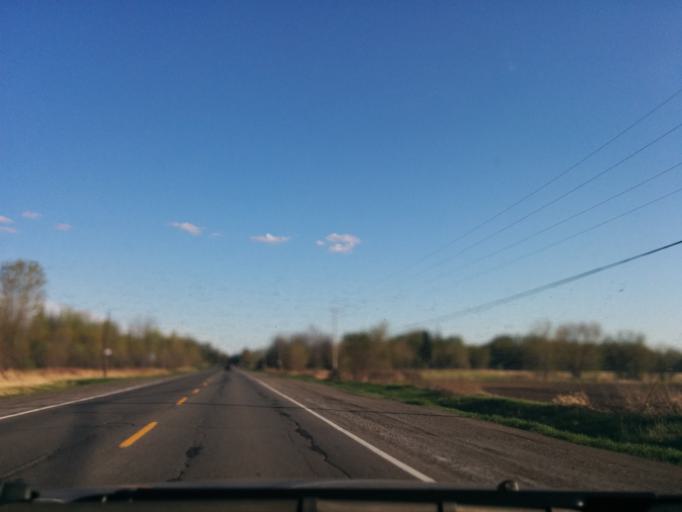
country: CA
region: Ontario
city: Bells Corners
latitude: 45.2619
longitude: -75.7003
